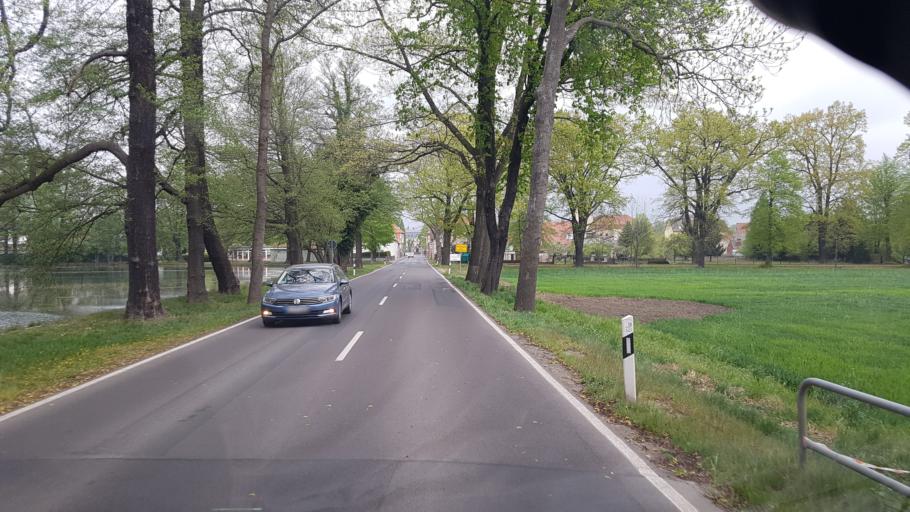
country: DE
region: Brandenburg
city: Altdobern
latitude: 51.6483
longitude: 14.0343
